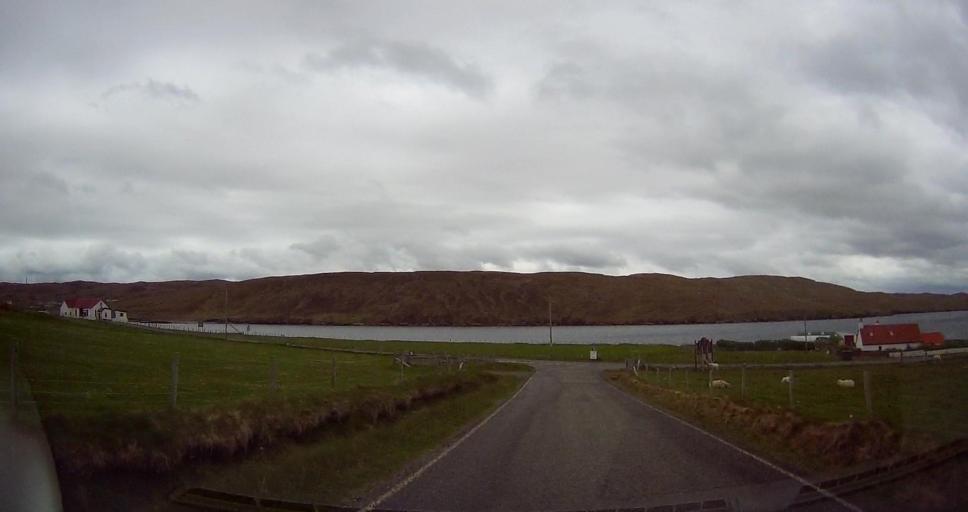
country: GB
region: Scotland
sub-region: Shetland Islands
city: Lerwick
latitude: 60.4835
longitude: -1.4748
